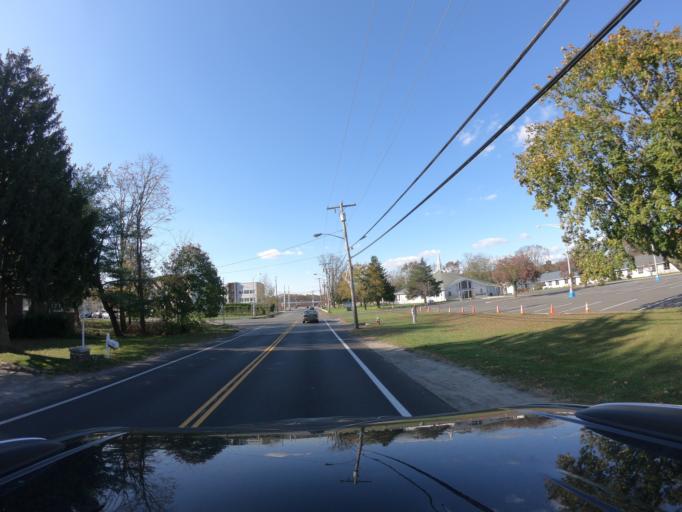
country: US
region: New Jersey
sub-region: Monmouth County
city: Ramtown
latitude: 40.1024
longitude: -74.1728
